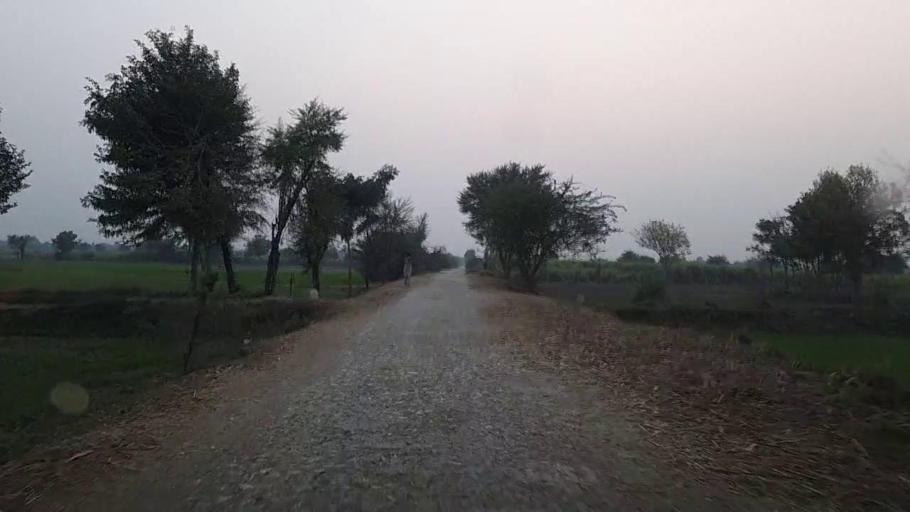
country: PK
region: Sindh
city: Kandiari
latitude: 26.9717
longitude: 68.4751
